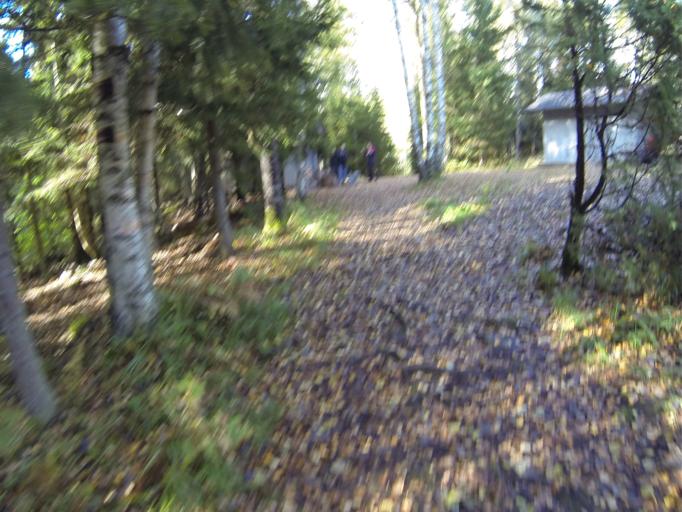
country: FI
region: Haeme
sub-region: Forssa
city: Forssa
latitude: 60.7361
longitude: 23.5808
